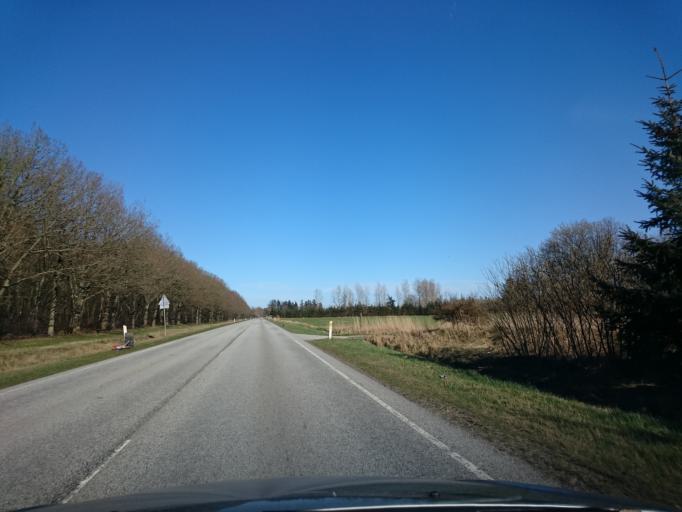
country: DK
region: North Denmark
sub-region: Hjorring Kommune
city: Sindal
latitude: 57.5880
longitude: 10.2678
